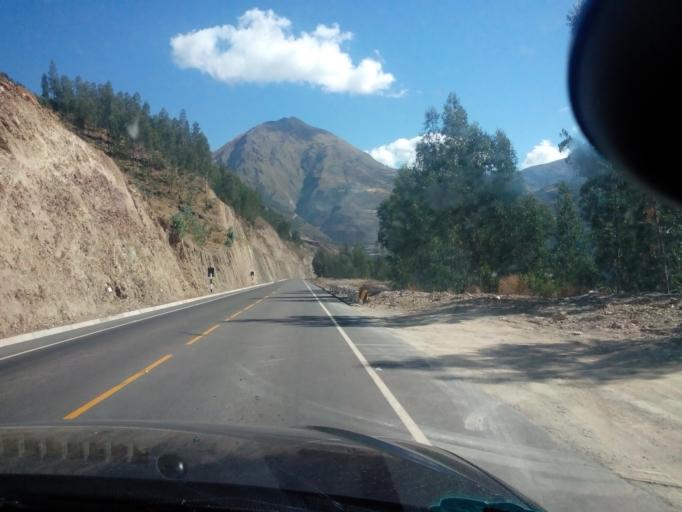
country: PE
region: Cusco
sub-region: Provincia de Quispicanchis
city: Urcos
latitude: -13.6844
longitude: -71.6269
